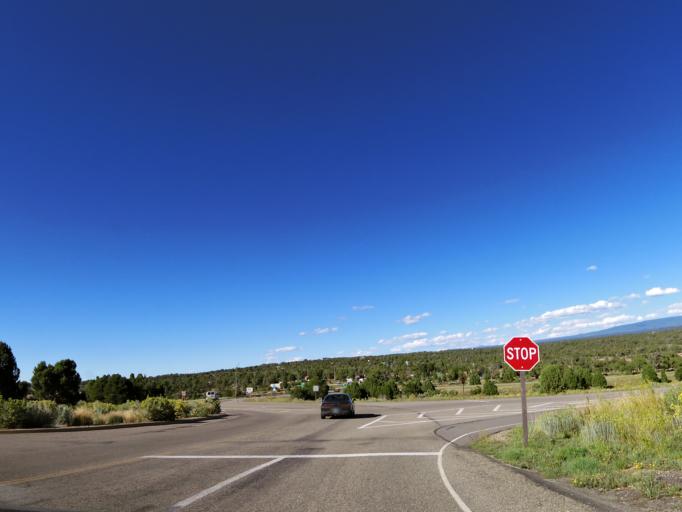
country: US
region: Colorado
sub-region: Montezuma County
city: Mancos
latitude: 37.3388
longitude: -108.4120
